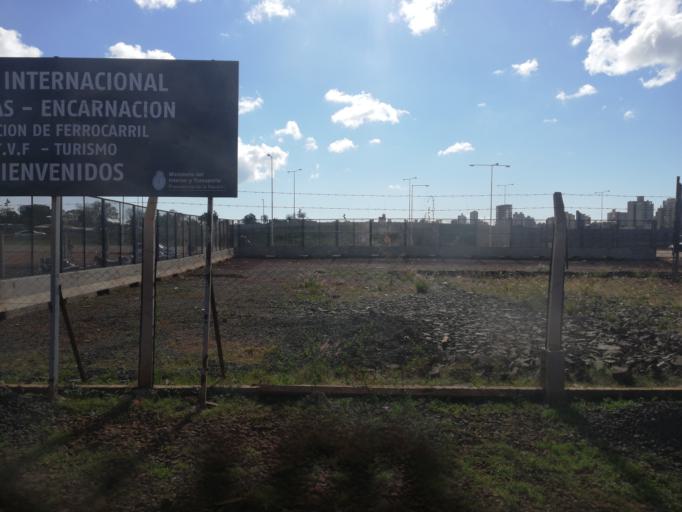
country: AR
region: Misiones
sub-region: Departamento de Capital
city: Posadas
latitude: -27.3798
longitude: -55.8837
